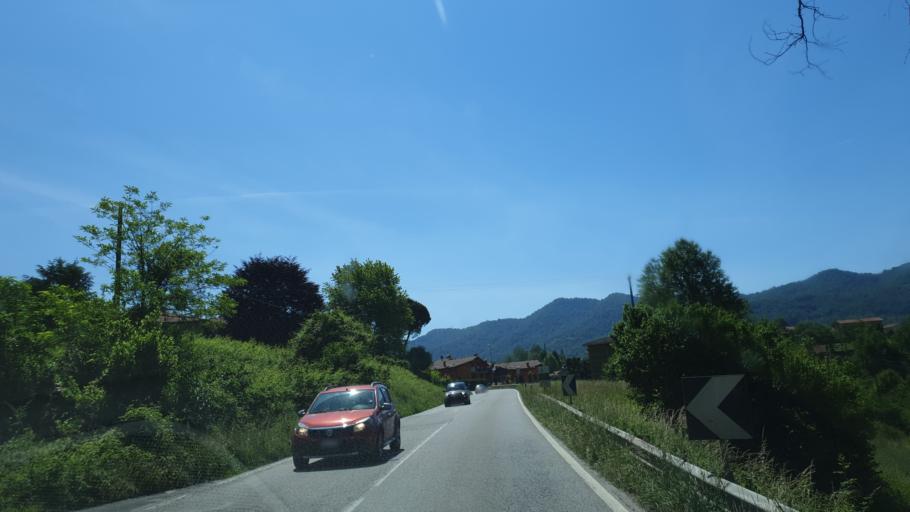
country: IT
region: Lombardy
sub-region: Provincia di Bergamo
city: Cisano Bergamasco
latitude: 45.7504
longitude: 9.4654
